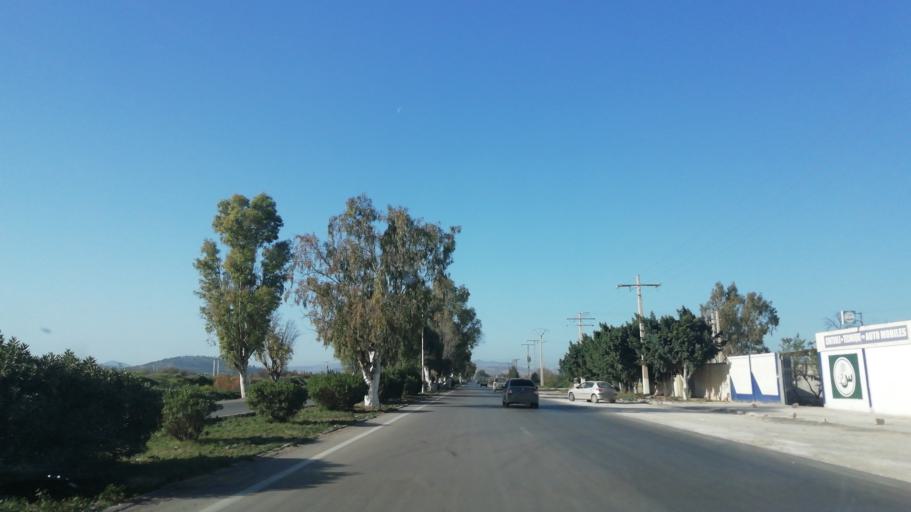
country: DZ
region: Mascara
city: Mascara
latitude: 35.6096
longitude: 0.0968
